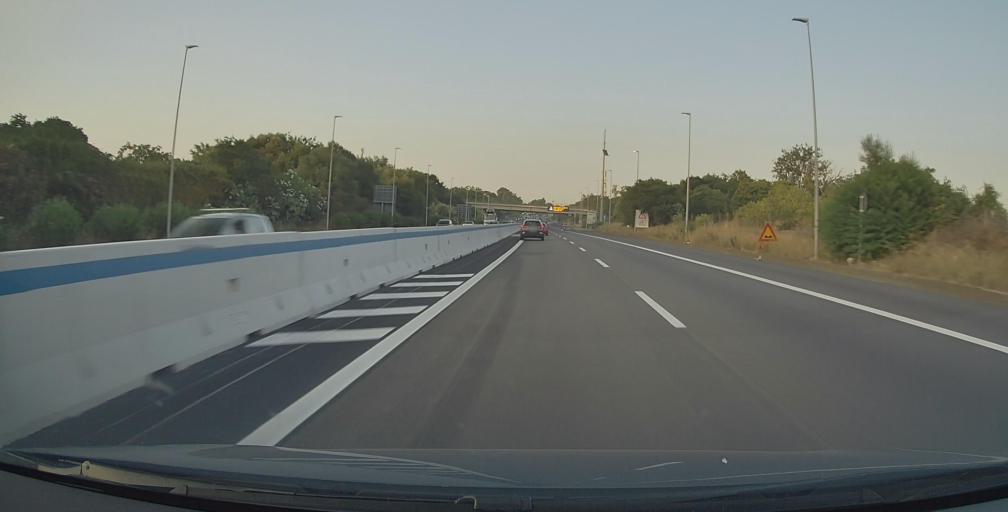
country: IT
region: Sicily
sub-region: Catania
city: Sant'Agata Li Battiati
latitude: 37.5594
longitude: 15.0929
